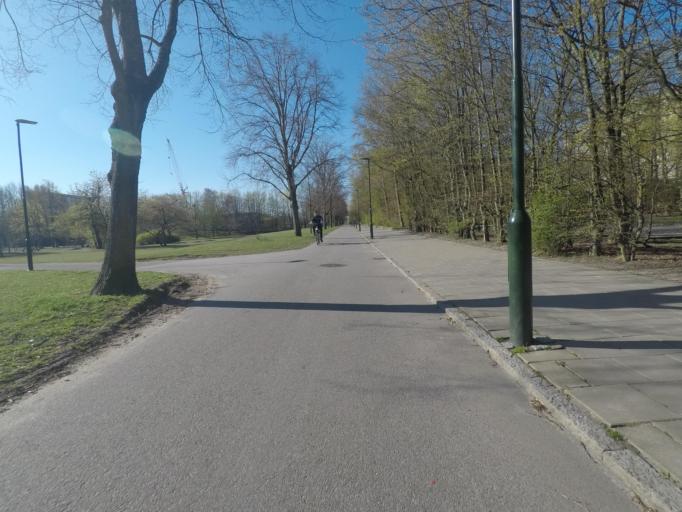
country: SE
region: Skane
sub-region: Malmo
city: Malmoe
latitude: 55.5624
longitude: 13.0134
